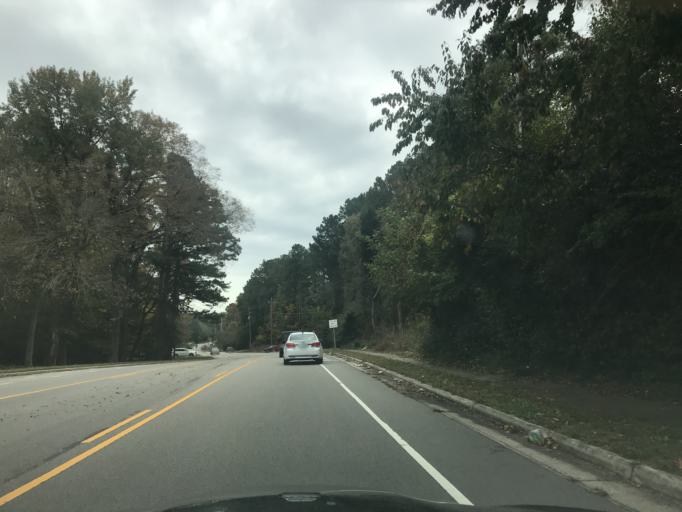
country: US
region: North Carolina
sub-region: Wake County
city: West Raleigh
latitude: 35.8784
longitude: -78.5975
